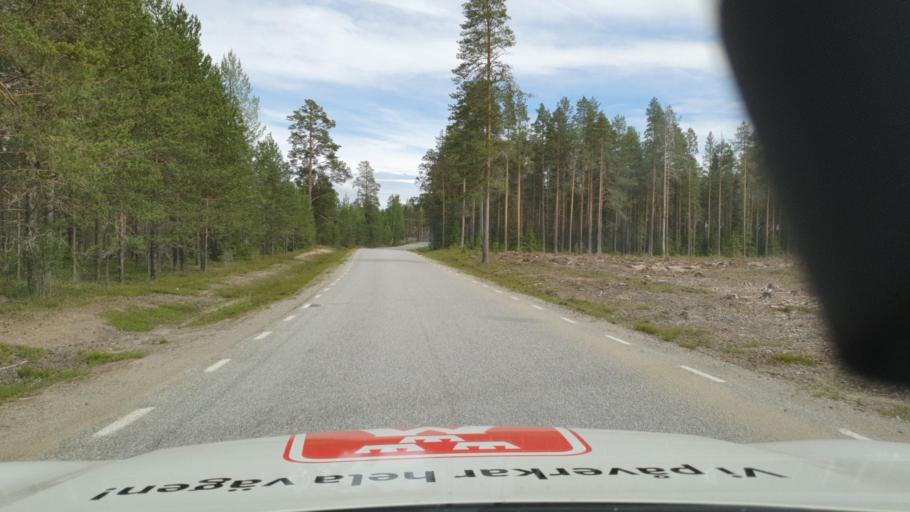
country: SE
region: Vaesterbotten
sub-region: Skelleftea Kommun
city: Burtraesk
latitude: 64.5010
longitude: 20.8428
